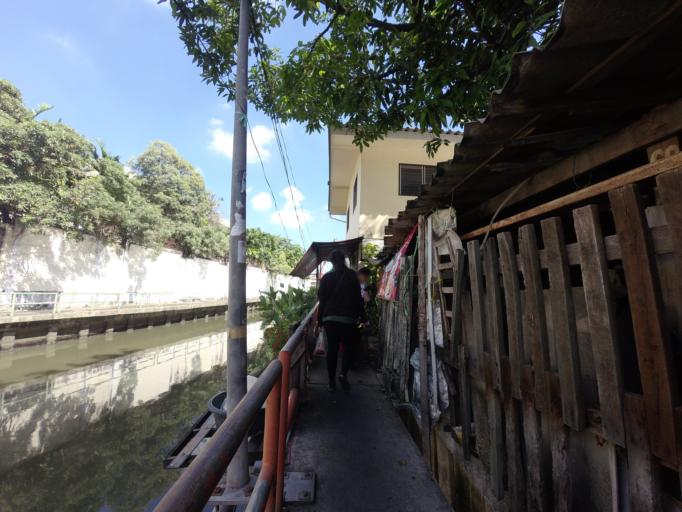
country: TH
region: Bangkok
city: Huai Khwang
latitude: 13.7896
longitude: 100.5899
